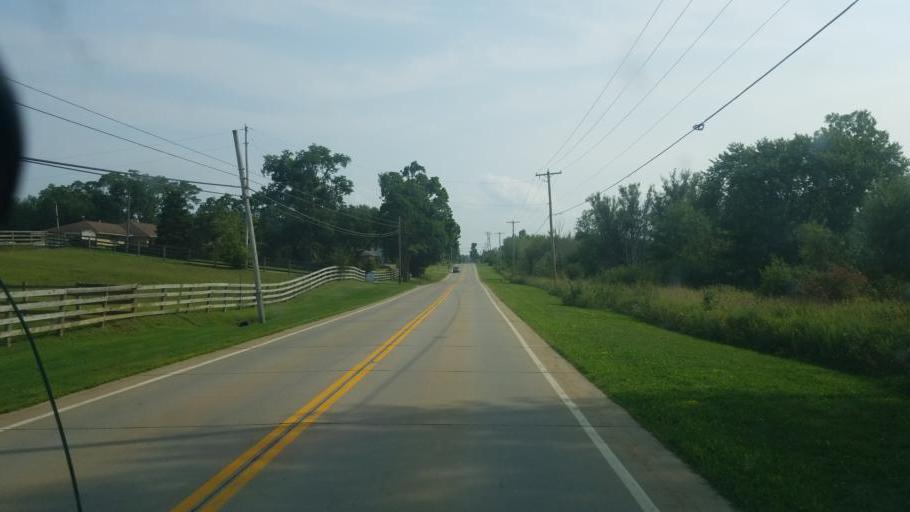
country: US
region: Ohio
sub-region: Medina County
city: Medina
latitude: 41.1043
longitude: -81.8840
